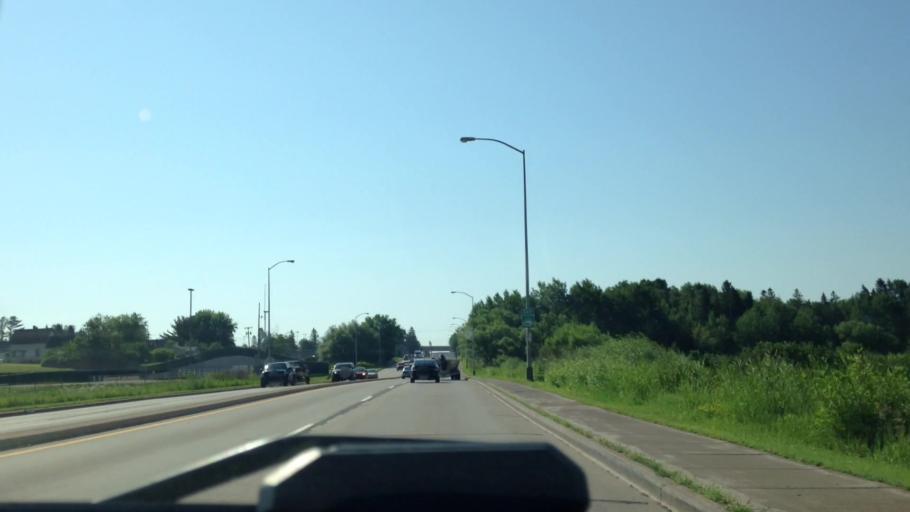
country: US
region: Wisconsin
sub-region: Douglas County
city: Superior
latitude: 46.6945
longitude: -92.0320
